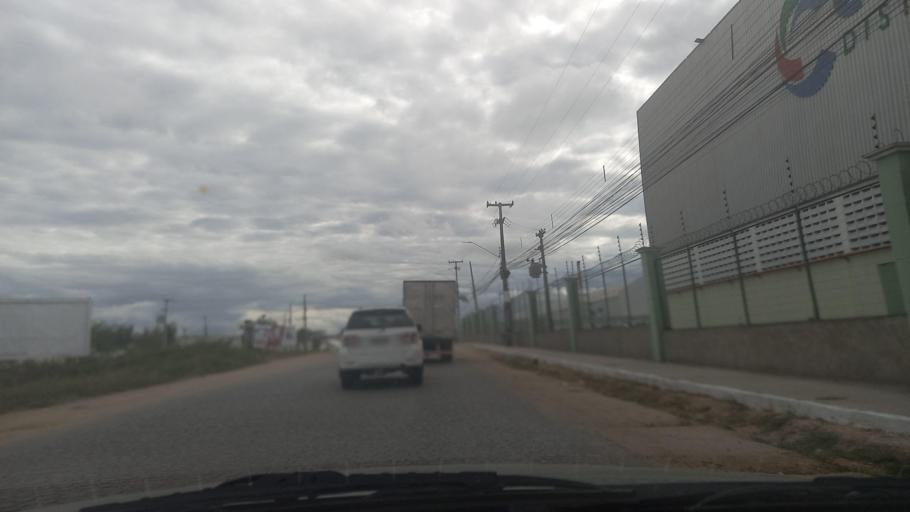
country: BR
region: Pernambuco
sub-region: Caruaru
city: Caruaru
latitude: -8.2887
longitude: -36.0112
